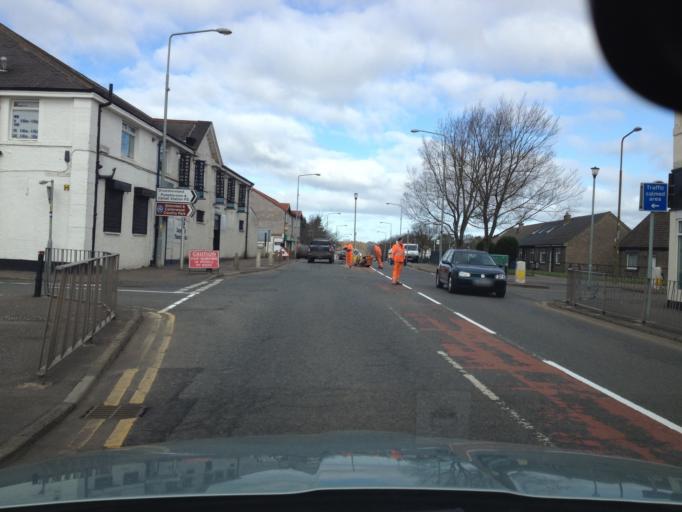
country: GB
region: Scotland
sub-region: West Lothian
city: Mid Calder
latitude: 55.9078
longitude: -3.4937
